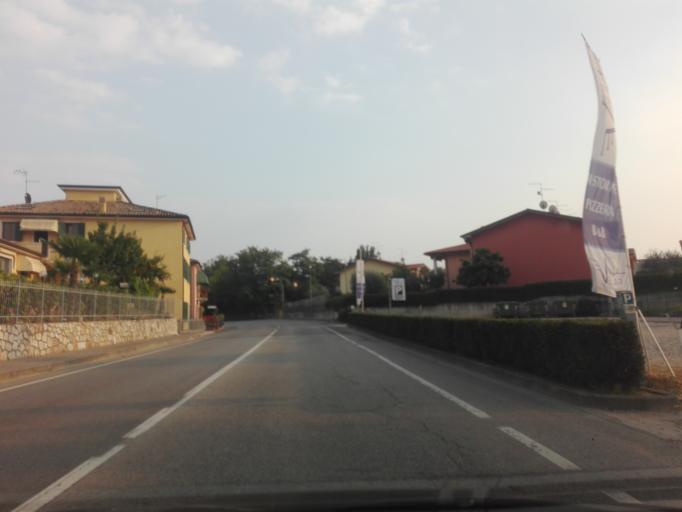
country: IT
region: Veneto
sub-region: Provincia di Verona
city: Lazise
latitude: 45.5002
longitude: 10.7476
